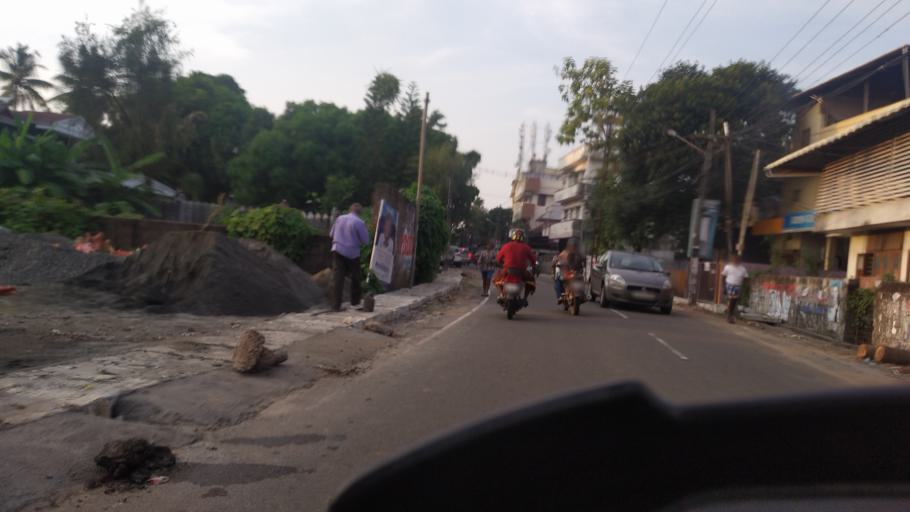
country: IN
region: Kerala
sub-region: Ernakulam
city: Elur
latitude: 10.0149
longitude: 76.2855
